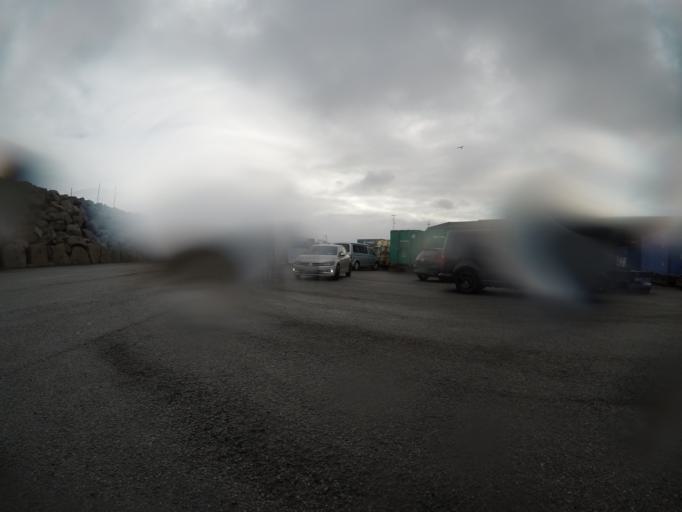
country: FO
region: Streymoy
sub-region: Torshavn
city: Torshavn
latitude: 62.0063
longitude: -6.7630
